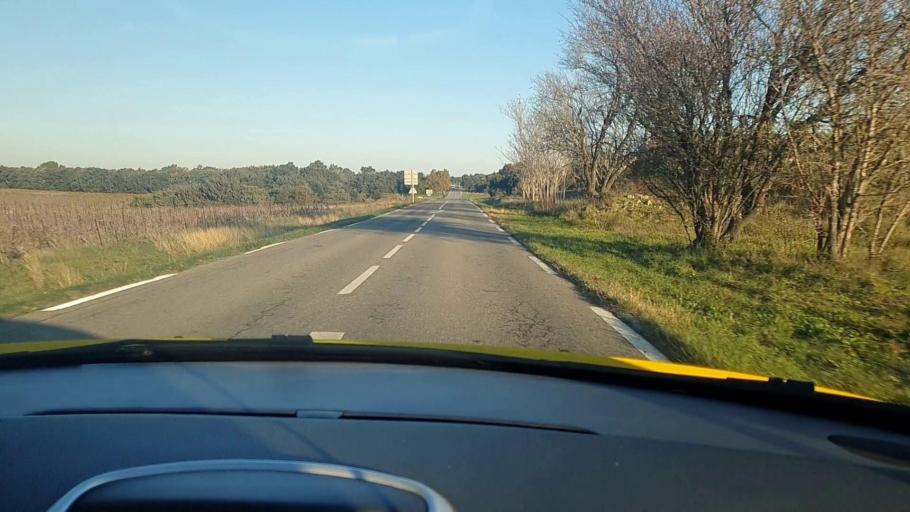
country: FR
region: Languedoc-Roussillon
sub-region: Departement du Gard
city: Montaren-et-Saint-Mediers
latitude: 44.0855
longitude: 4.3906
